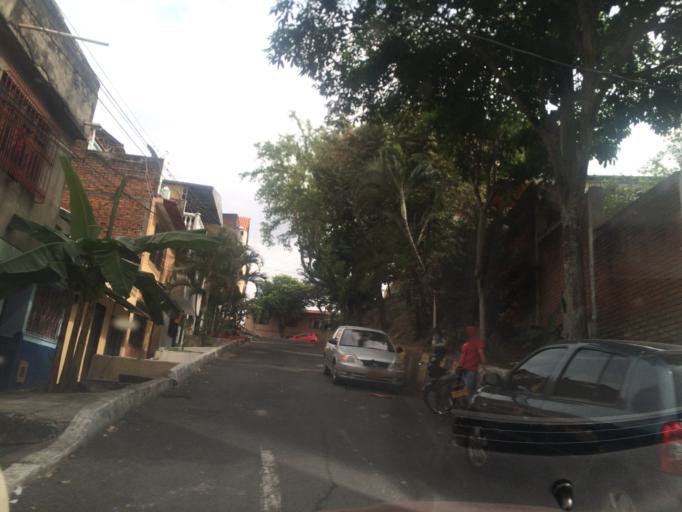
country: CO
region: Valle del Cauca
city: Cali
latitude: 3.4448
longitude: -76.5430
